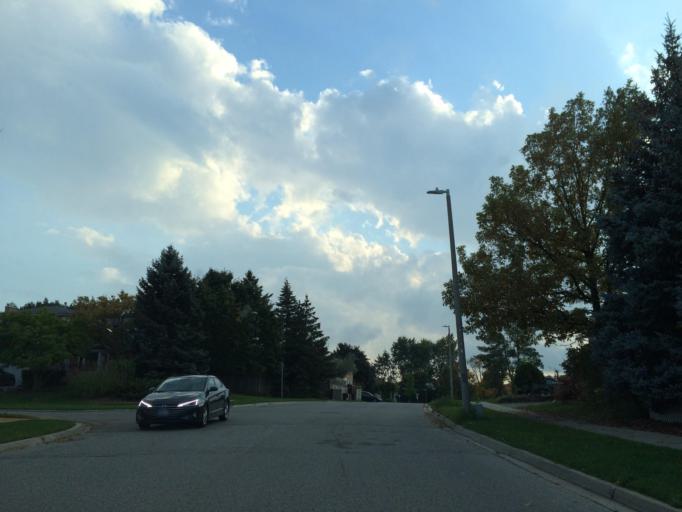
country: CA
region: Ontario
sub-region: Wellington County
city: Guelph
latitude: 43.5247
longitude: -80.2740
